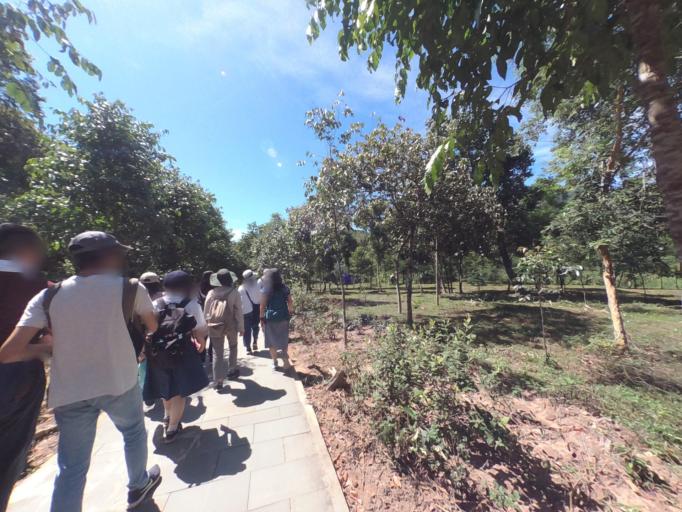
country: VN
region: Quang Nam
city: Dai Loc
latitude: 15.7668
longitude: 108.1219
